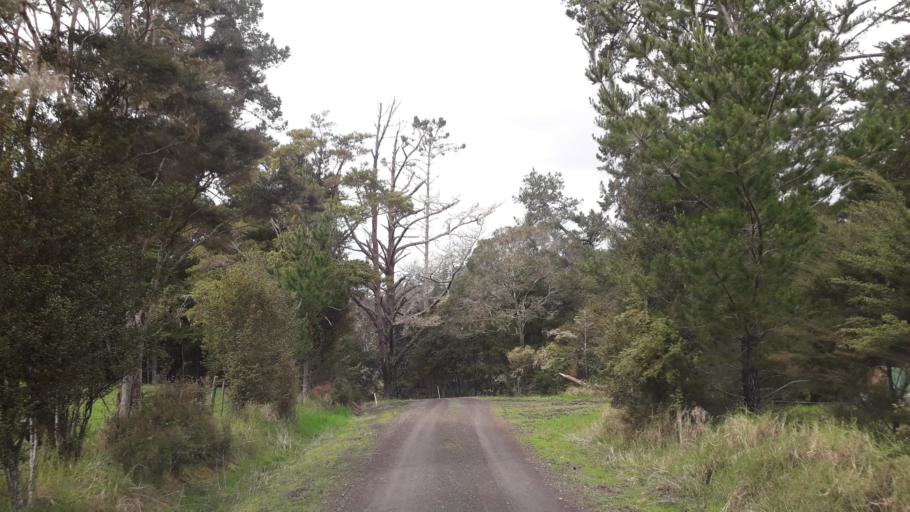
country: NZ
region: Northland
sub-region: Far North District
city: Waimate North
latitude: -35.3189
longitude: 173.5760
